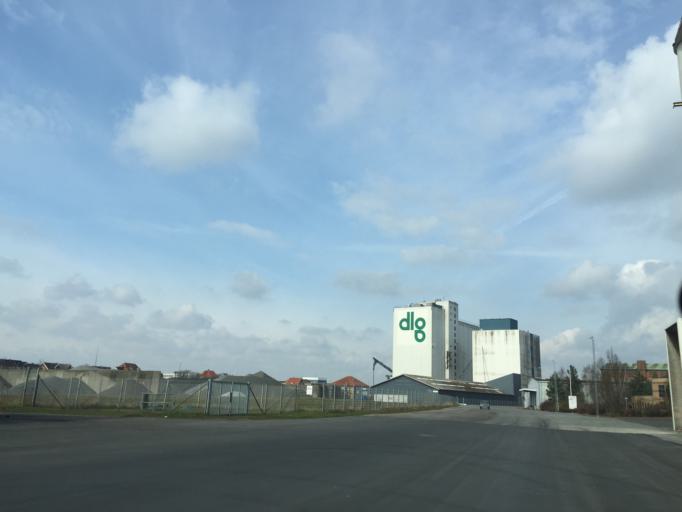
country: DK
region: South Denmark
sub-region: Odense Kommune
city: Odense
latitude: 55.4143
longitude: 10.3812
